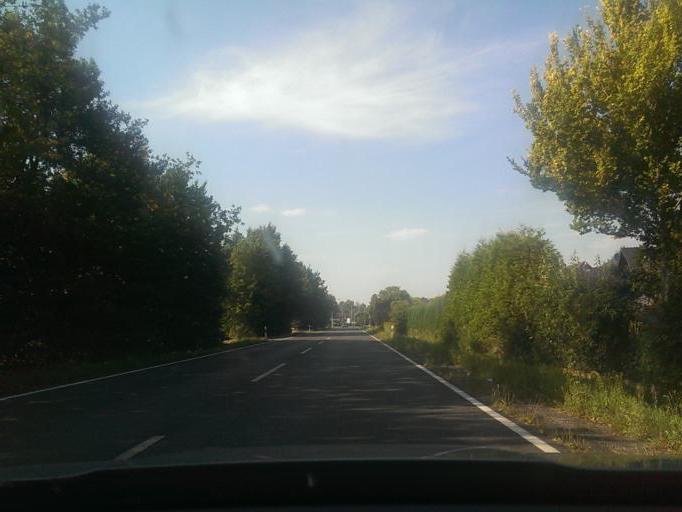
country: DE
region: North Rhine-Westphalia
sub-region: Regierungsbezirk Detmold
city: Delbruck
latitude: 51.7534
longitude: 8.5625
